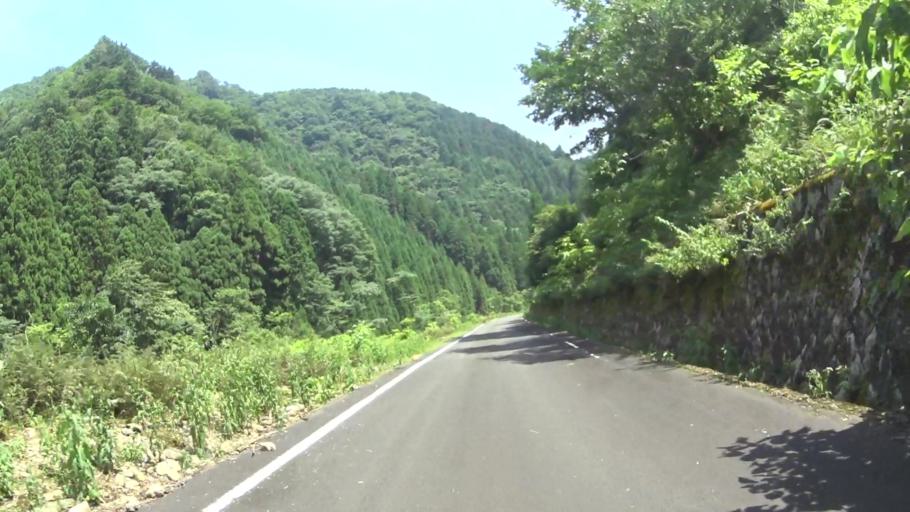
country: JP
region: Kyoto
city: Maizuru
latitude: 35.3493
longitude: 135.5220
